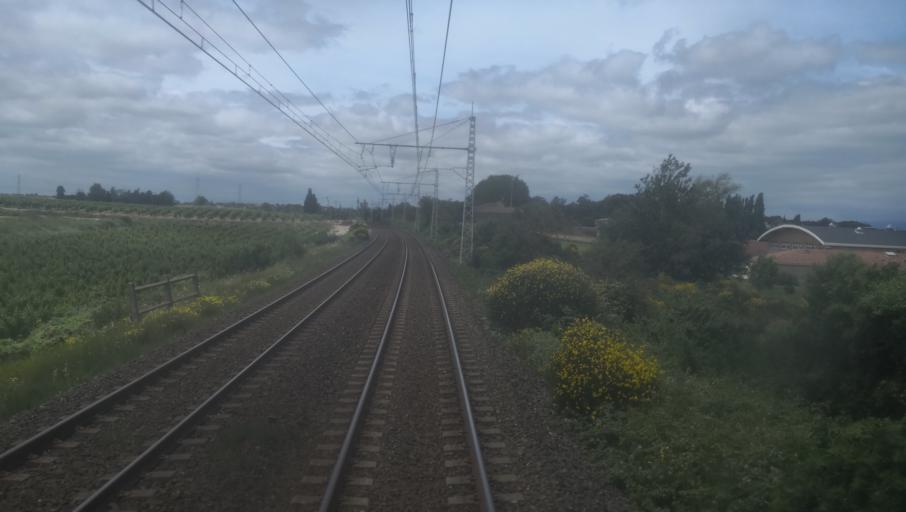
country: FR
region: Languedoc-Roussillon
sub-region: Departement de l'Aude
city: Villemoustaussou
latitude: 43.2186
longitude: 2.3933
